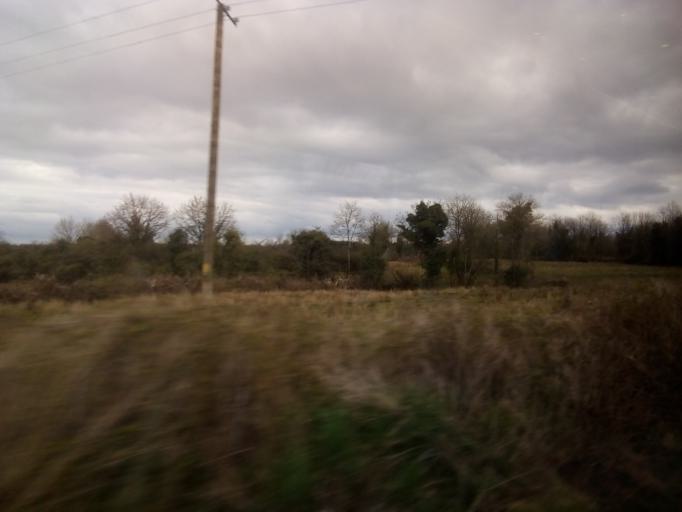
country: IE
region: Leinster
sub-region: An Longfort
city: Edgeworthstown
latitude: 53.6847
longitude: -7.5794
